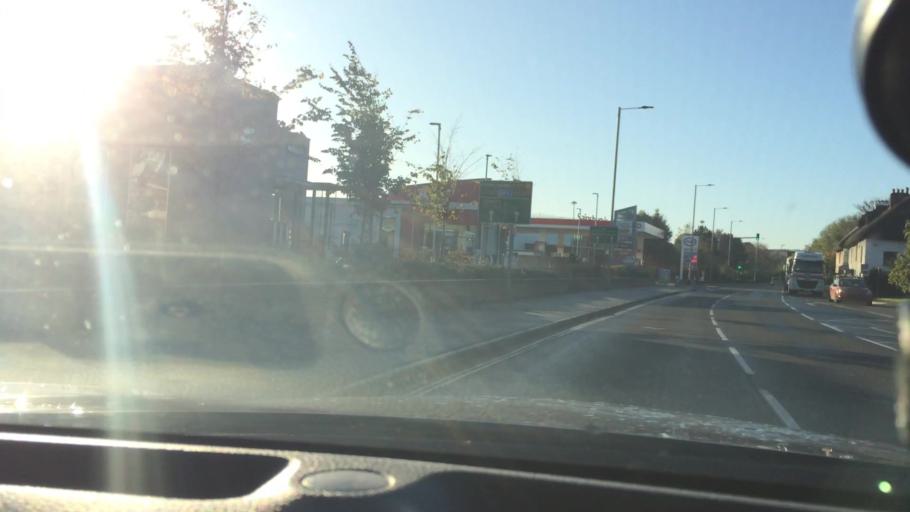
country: GB
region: England
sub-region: Devon
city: Exeter
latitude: 50.7082
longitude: -3.5375
